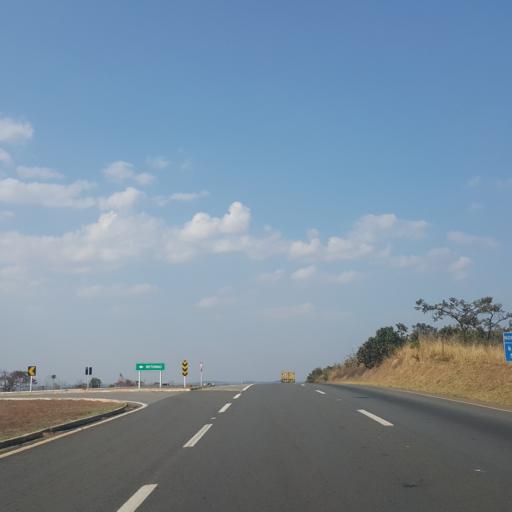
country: BR
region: Goias
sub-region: Abadiania
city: Abadiania
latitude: -16.1862
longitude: -48.6611
